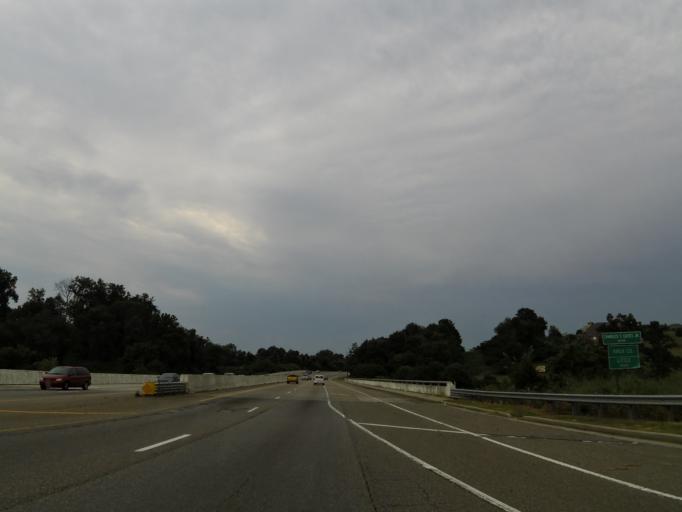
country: US
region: Tennessee
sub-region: Blount County
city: Eagleton Village
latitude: 35.8727
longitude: -83.9591
